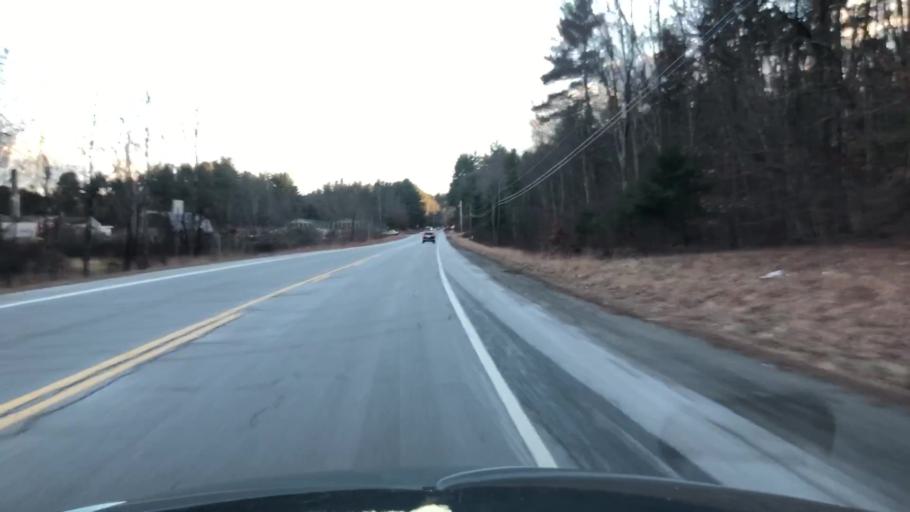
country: US
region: New Hampshire
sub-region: Hillsborough County
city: Brookline
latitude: 42.7228
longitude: -71.6625
